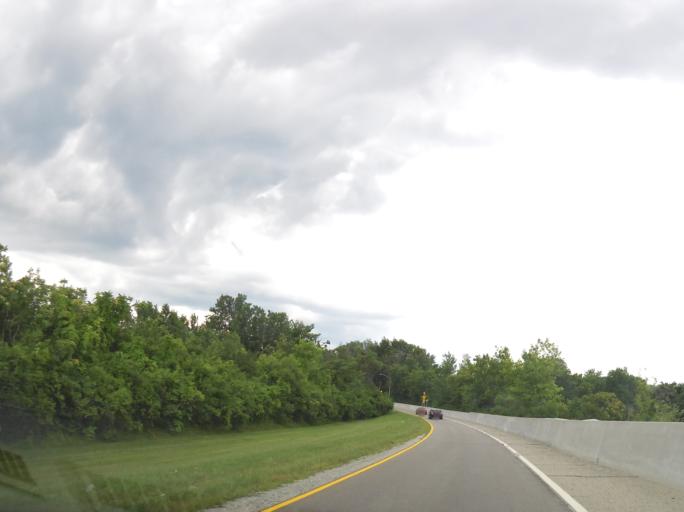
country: US
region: Ohio
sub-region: Montgomery County
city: Riverside
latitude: 39.7958
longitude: -84.0930
